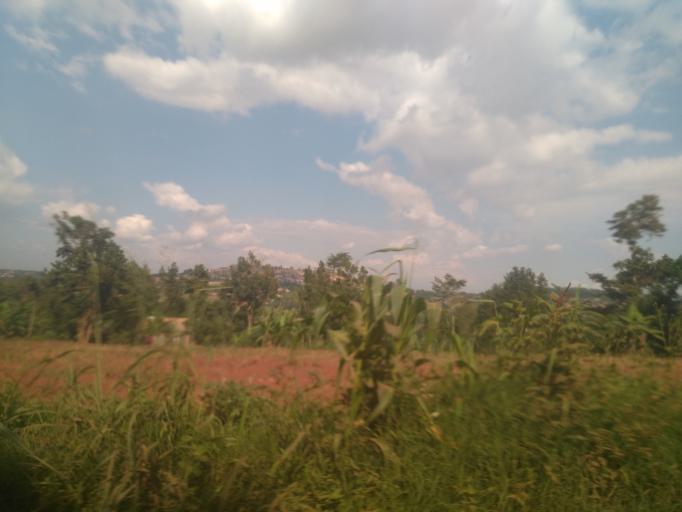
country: UG
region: Central Region
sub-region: Wakiso District
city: Kajansi
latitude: 0.2659
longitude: 32.4373
